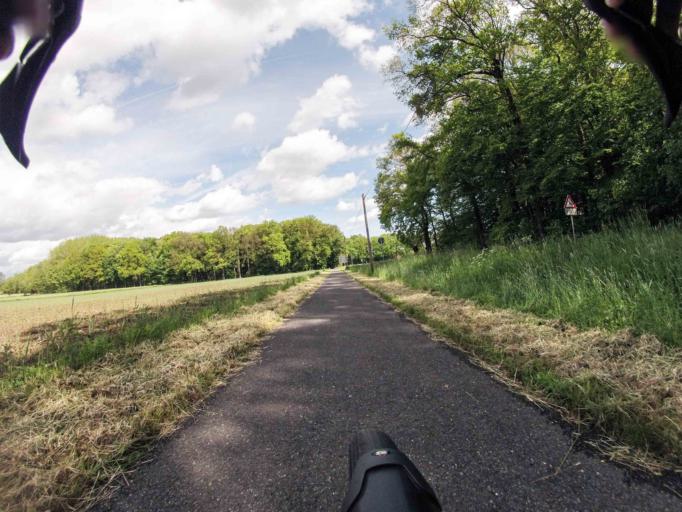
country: DE
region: North Rhine-Westphalia
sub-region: Regierungsbezirk Munster
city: Westerkappeln
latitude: 52.2799
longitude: 7.8638
